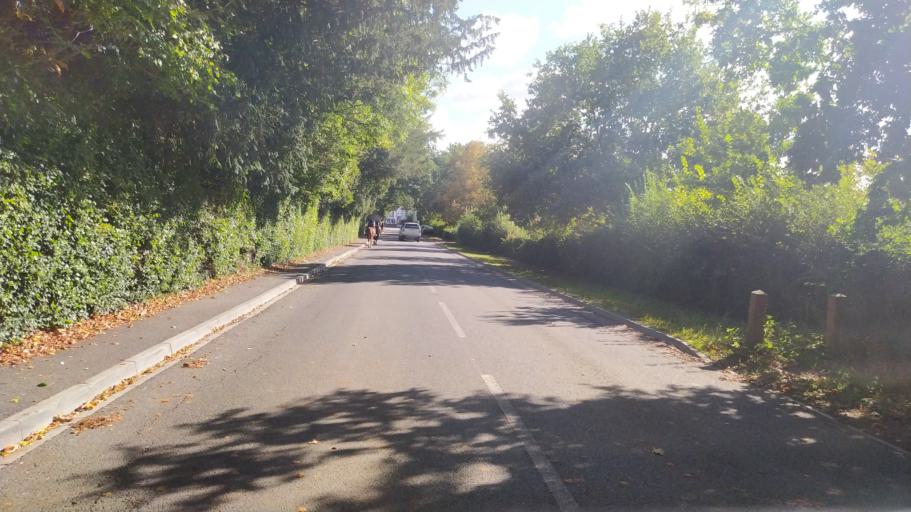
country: GB
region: England
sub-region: West Berkshire
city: Calcot
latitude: 51.4116
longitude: -1.0446
